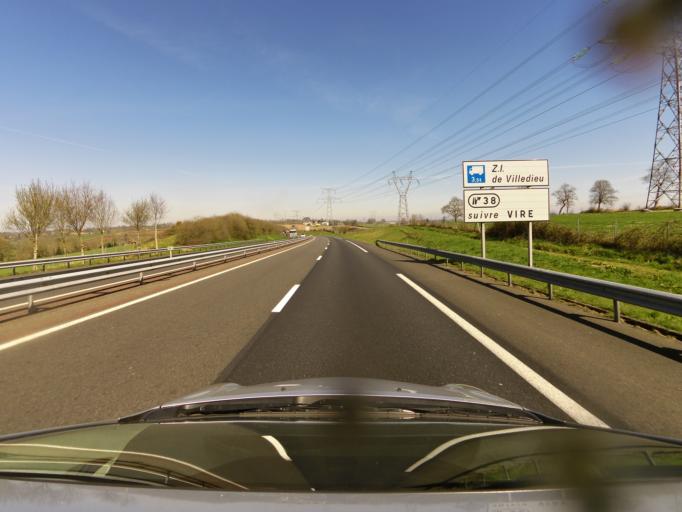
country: FR
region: Lower Normandy
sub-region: Departement de la Manche
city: Villedieu-les-Poeles
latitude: 48.8306
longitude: -1.2447
